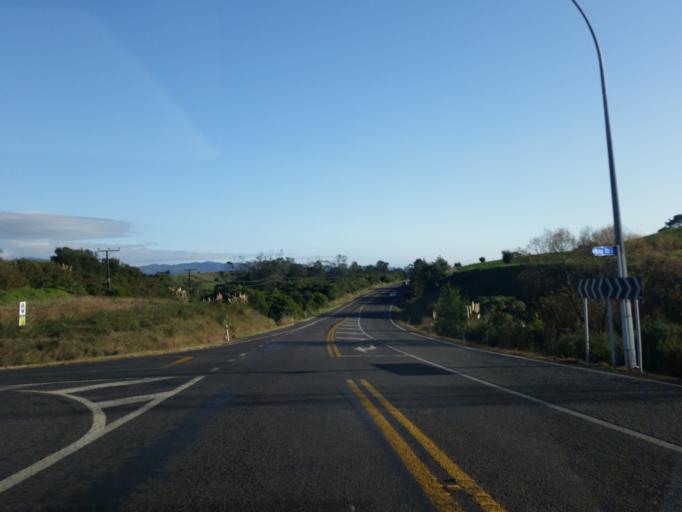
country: NZ
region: Bay of Plenty
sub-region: Western Bay of Plenty District
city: Katikati
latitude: -37.6481
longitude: 175.9668
